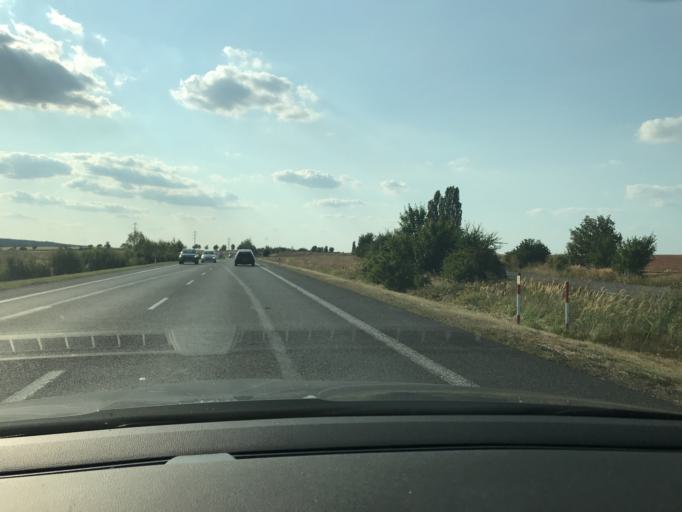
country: CZ
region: Central Bohemia
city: Klobuky
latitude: 50.2781
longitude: 13.9650
